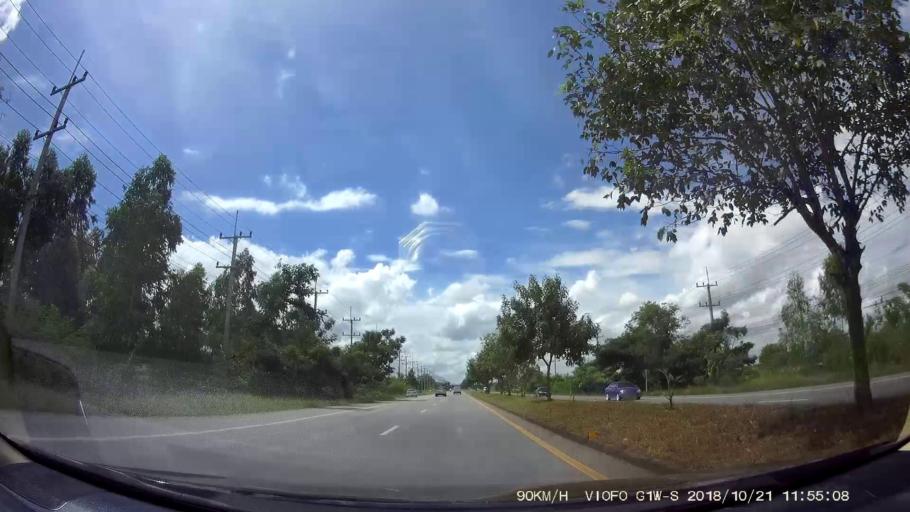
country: TH
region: Chaiyaphum
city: Chatturat
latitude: 15.5788
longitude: 101.8950
